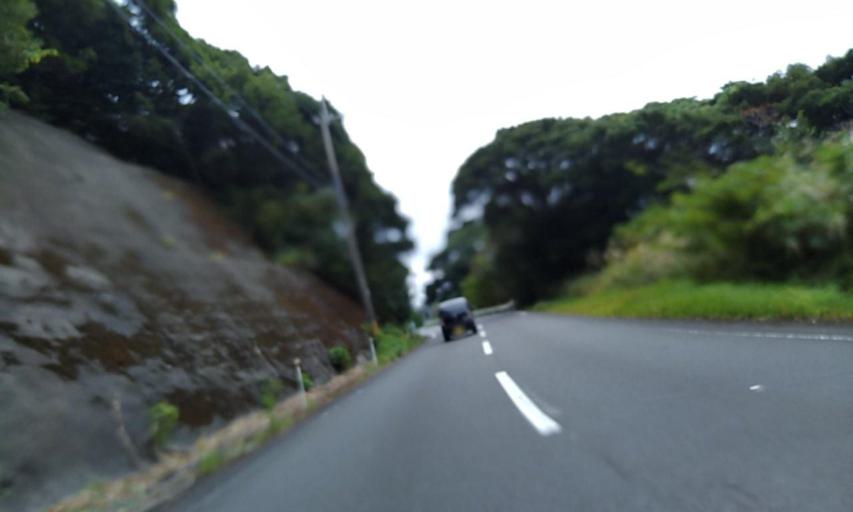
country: JP
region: Wakayama
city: Shingu
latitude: 33.4691
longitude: 135.8248
